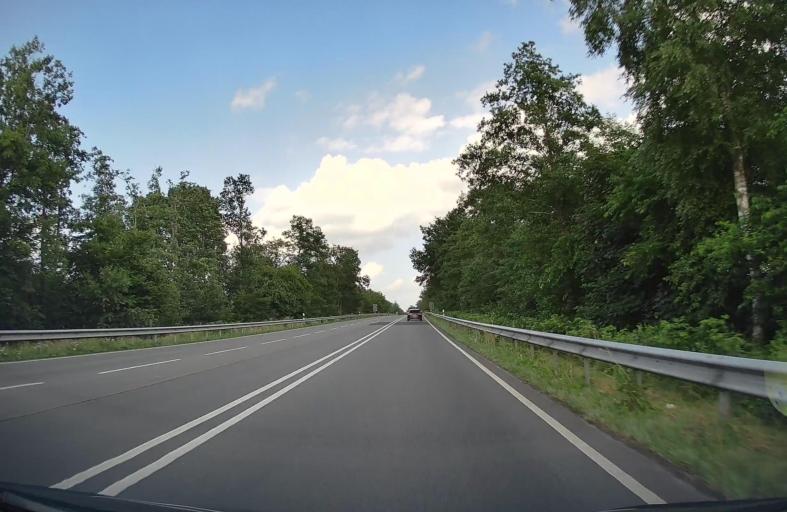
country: DE
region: Lower Saxony
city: Friesoythe
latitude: 53.0244
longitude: 7.8111
